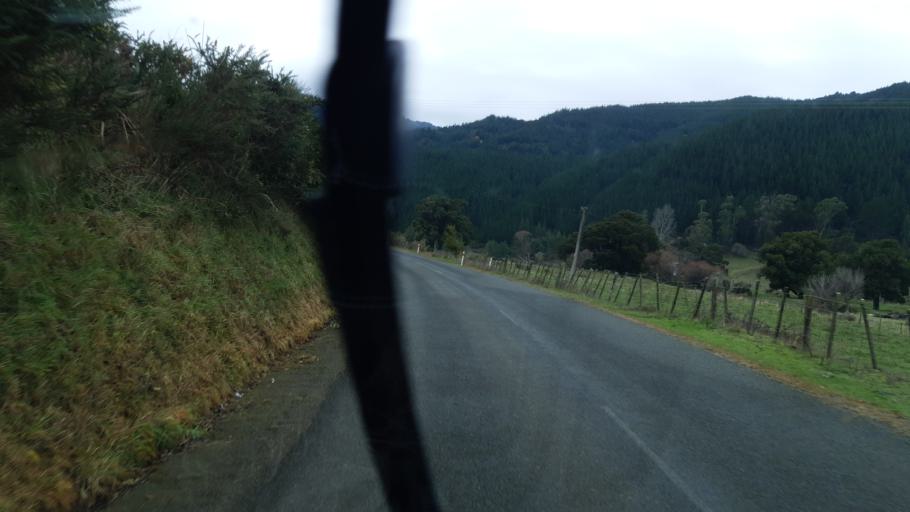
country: NZ
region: Nelson
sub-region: Nelson City
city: Nelson
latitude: -41.2036
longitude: 173.4078
